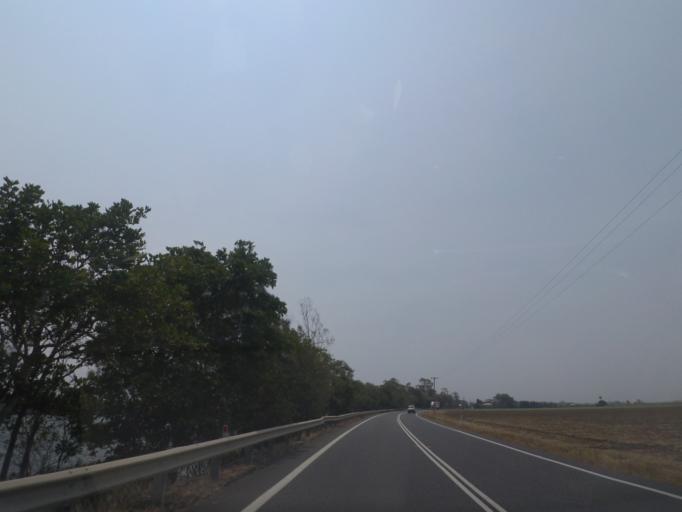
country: AU
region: New South Wales
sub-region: Richmond Valley
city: Evans Head
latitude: -28.9738
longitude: 153.4606
